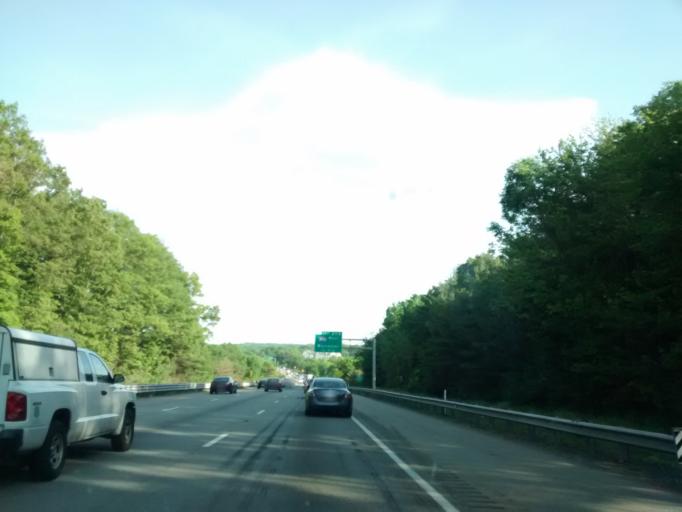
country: US
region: Massachusetts
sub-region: Middlesex County
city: Hudson
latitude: 42.3724
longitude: -71.5974
